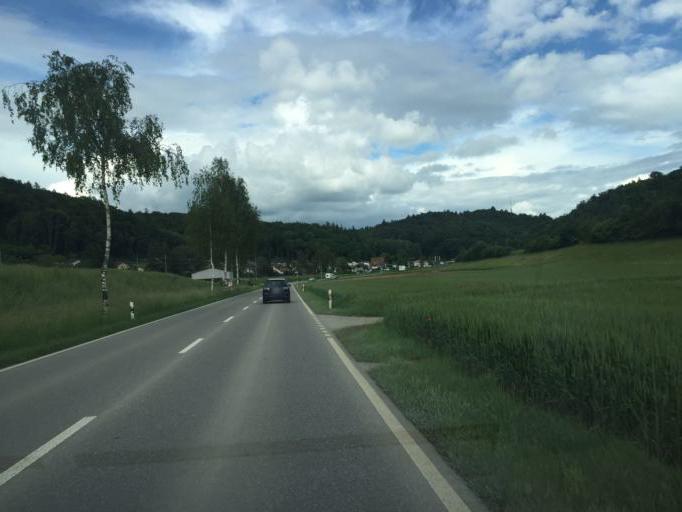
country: CH
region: Schaffhausen
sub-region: Bezirk Schaffhausen
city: Neuhausen
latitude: 47.6937
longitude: 8.5965
